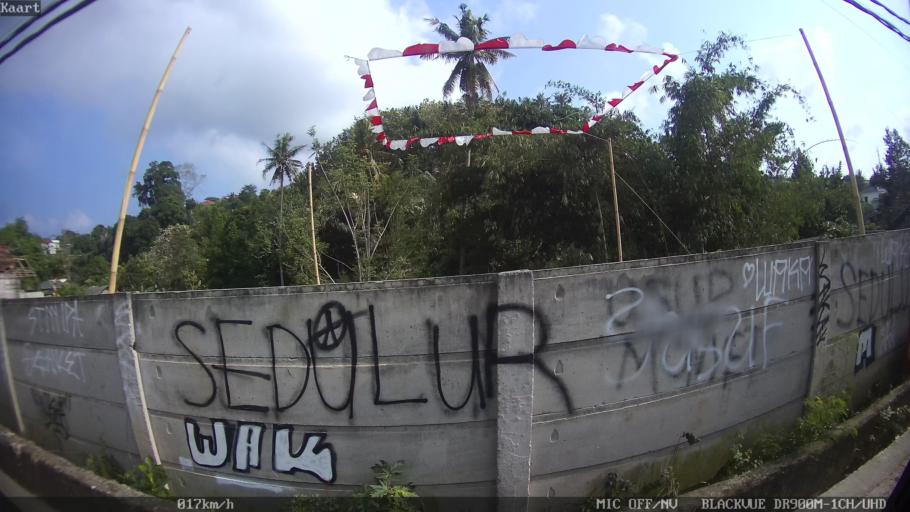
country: ID
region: Lampung
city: Bandarlampung
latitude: -5.4297
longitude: 105.2482
